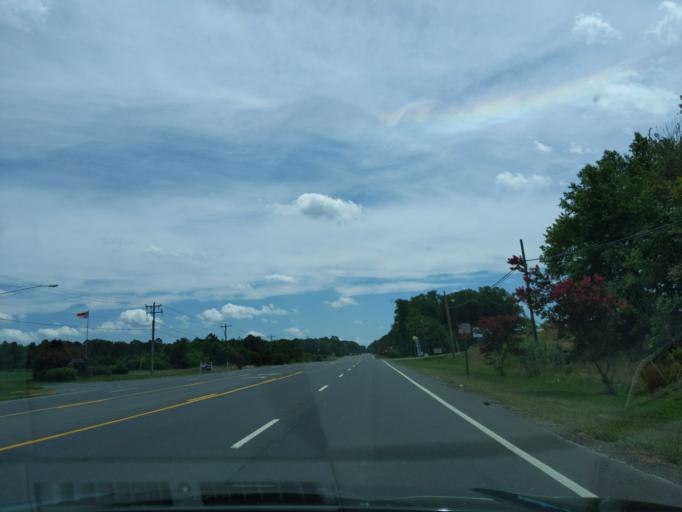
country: US
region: North Carolina
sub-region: Stanly County
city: Albemarle
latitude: 35.4652
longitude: -80.2541
